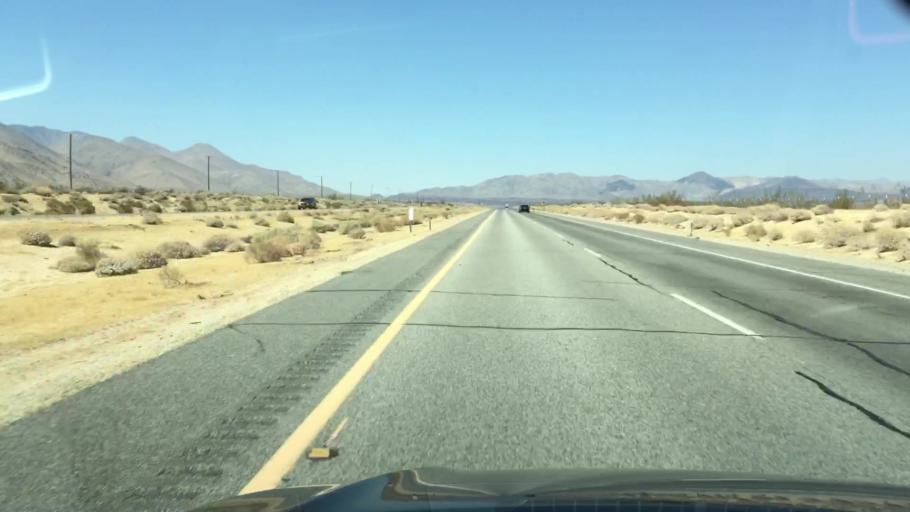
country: US
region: California
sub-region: Kern County
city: Inyokern
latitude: 35.7651
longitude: -117.8710
